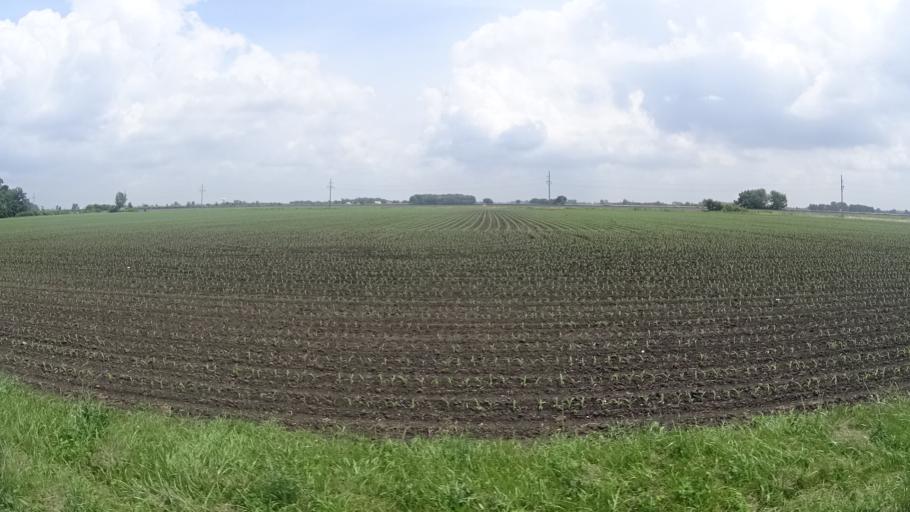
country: US
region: Ohio
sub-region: Huron County
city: Bellevue
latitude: 41.3201
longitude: -82.8052
